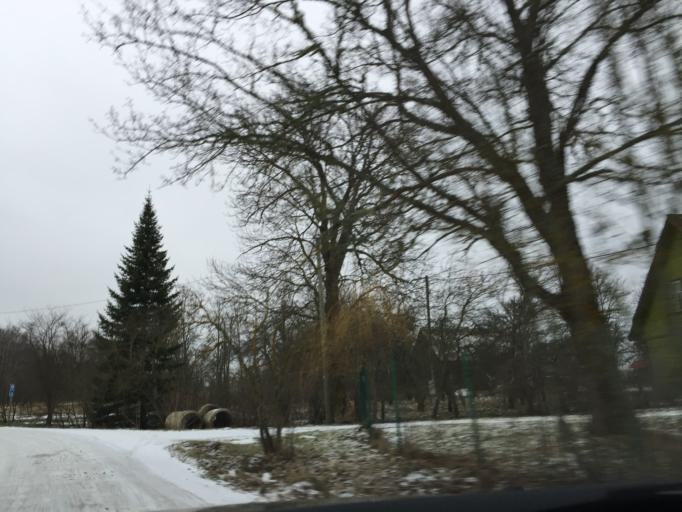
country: LV
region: Saulkrastu
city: Saulkrasti
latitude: 57.5073
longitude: 24.3824
